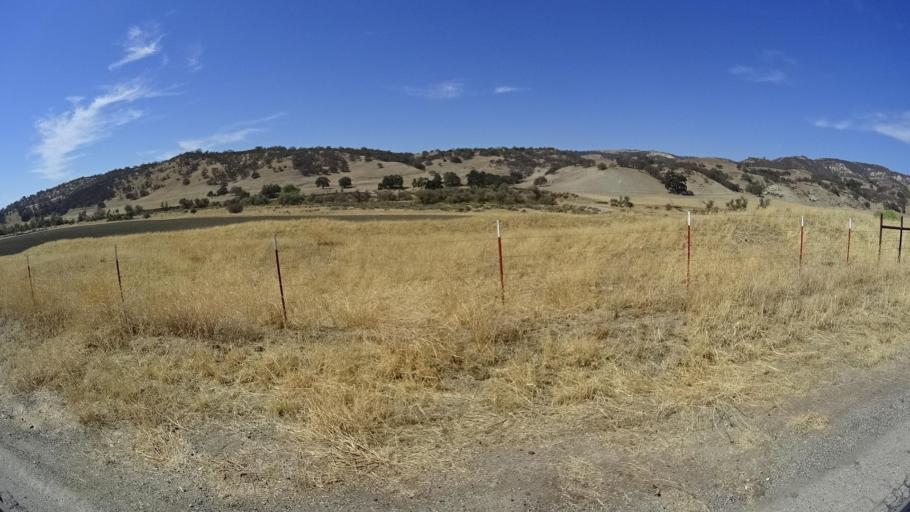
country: US
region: California
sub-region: San Luis Obispo County
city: San Miguel
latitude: 35.9292
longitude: -120.6783
